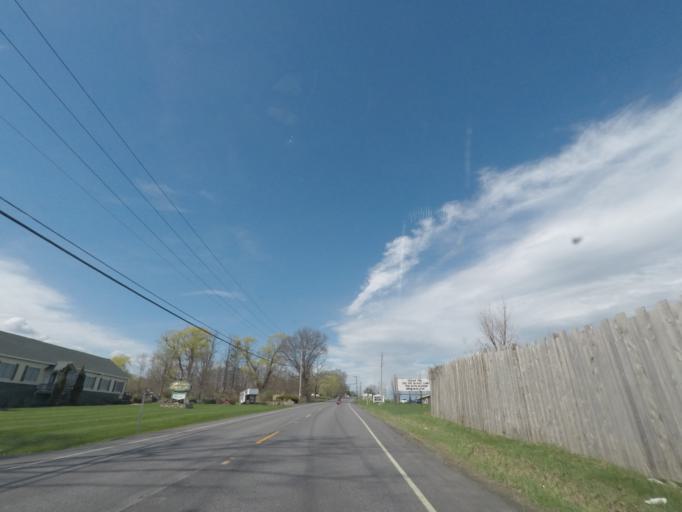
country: US
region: New York
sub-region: Greene County
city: Cairo
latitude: 42.3995
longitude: -74.0282
